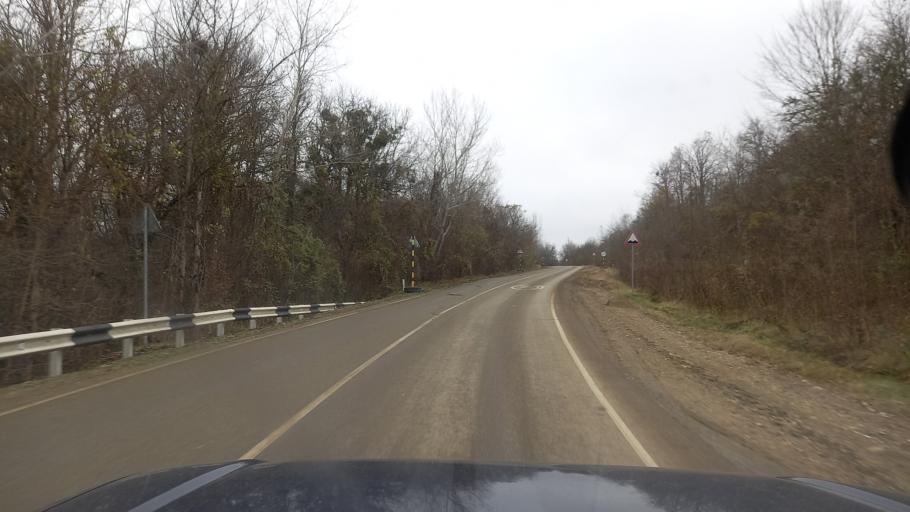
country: RU
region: Krasnodarskiy
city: Goryachiy Klyuch
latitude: 44.5550
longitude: 39.2523
